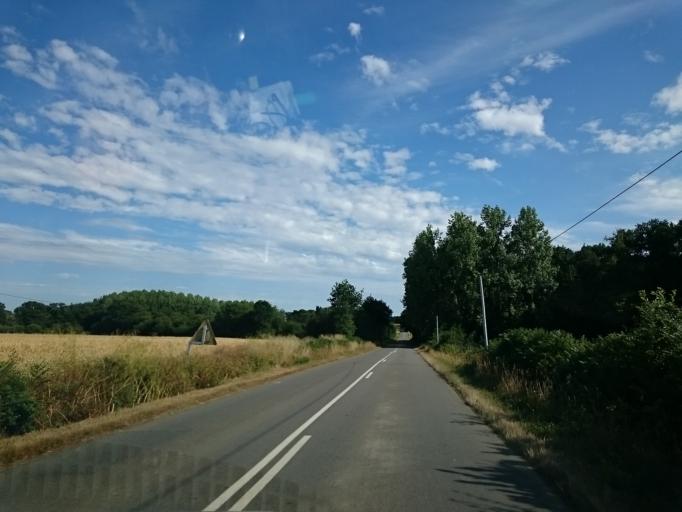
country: FR
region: Brittany
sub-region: Departement d'Ille-et-Vilaine
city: Chanteloup
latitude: 47.9159
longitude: -1.6177
